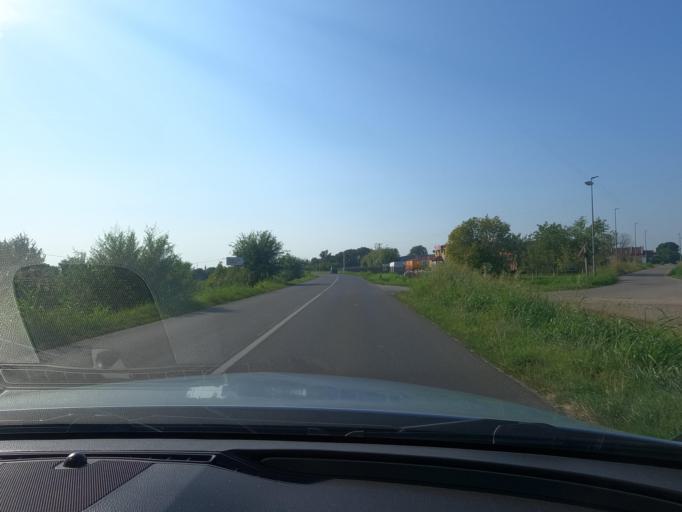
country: RS
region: Autonomna Pokrajina Vojvodina
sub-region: Juznobacki Okrug
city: Kovilj
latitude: 45.2908
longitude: 19.9627
